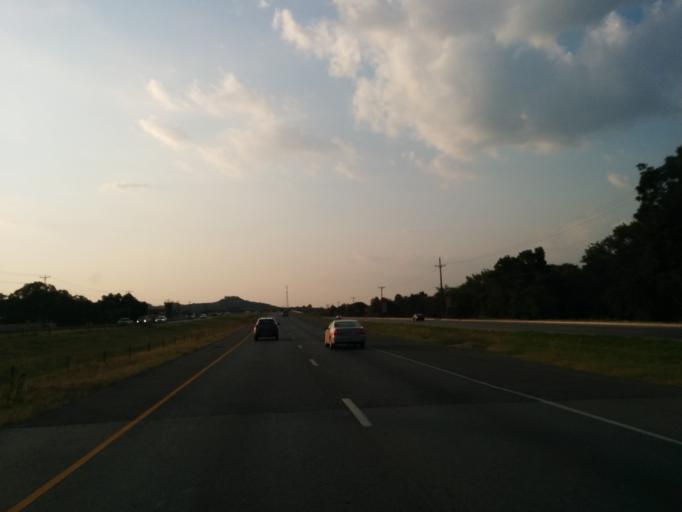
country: US
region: Texas
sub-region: Bexar County
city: Cross Mountain
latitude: 29.6442
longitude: -98.6197
